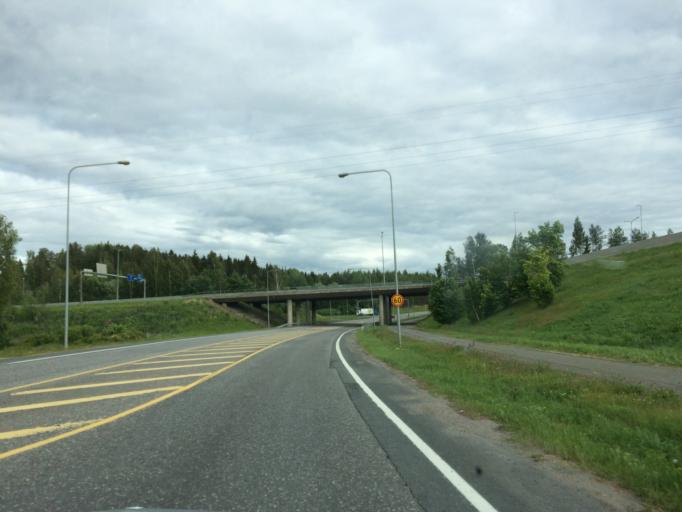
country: FI
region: Haeme
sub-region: Haemeenlinna
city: Haemeenlinna
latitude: 60.9733
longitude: 24.4751
